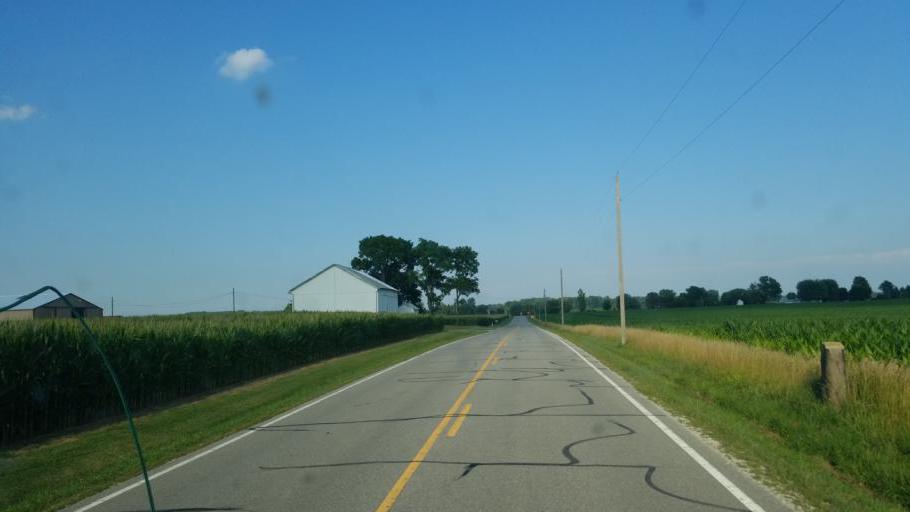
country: US
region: Ohio
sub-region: Crawford County
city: Galion
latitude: 40.7987
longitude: -82.8637
